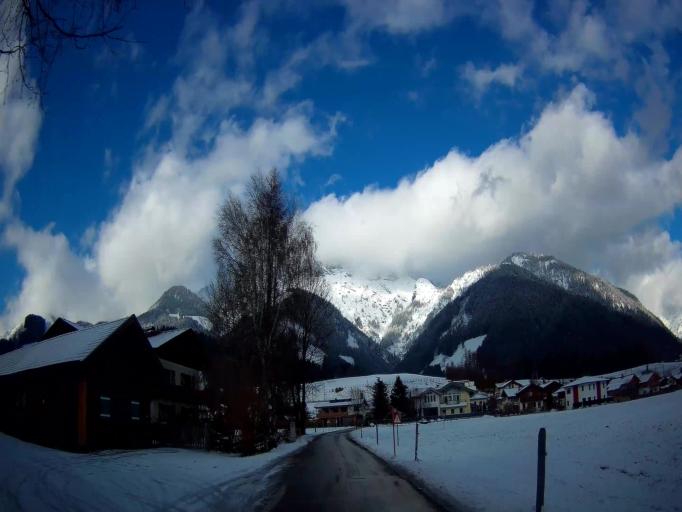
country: AT
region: Salzburg
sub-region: Politischer Bezirk Zell am See
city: Leogang
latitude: 47.4433
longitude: 12.7961
